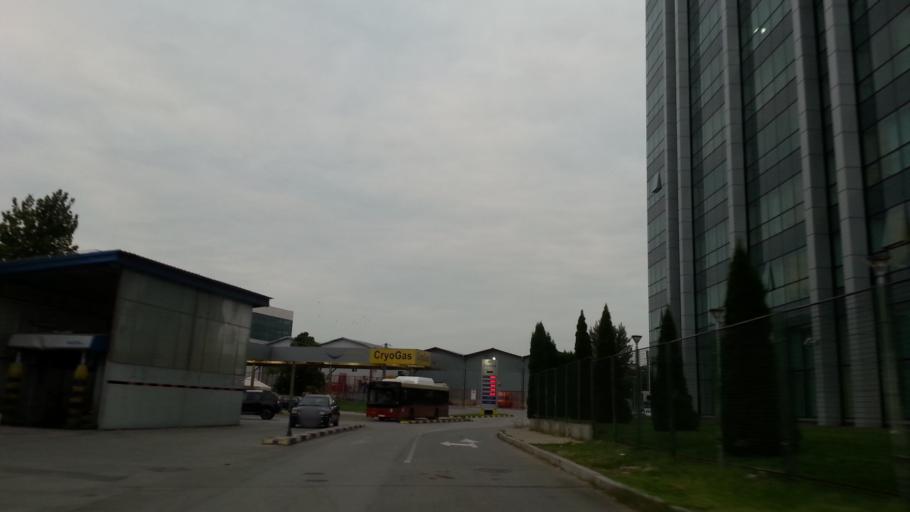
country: RS
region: Central Serbia
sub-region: Belgrade
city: Novi Beograd
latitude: 44.8116
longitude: 20.3959
